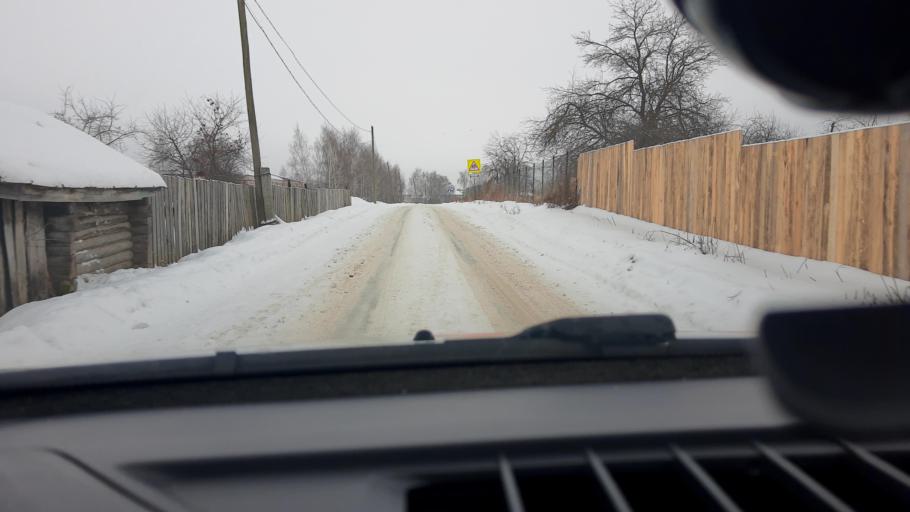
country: RU
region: Nizjnij Novgorod
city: Dal'neye Konstantinovo
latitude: 55.9265
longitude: 44.0559
